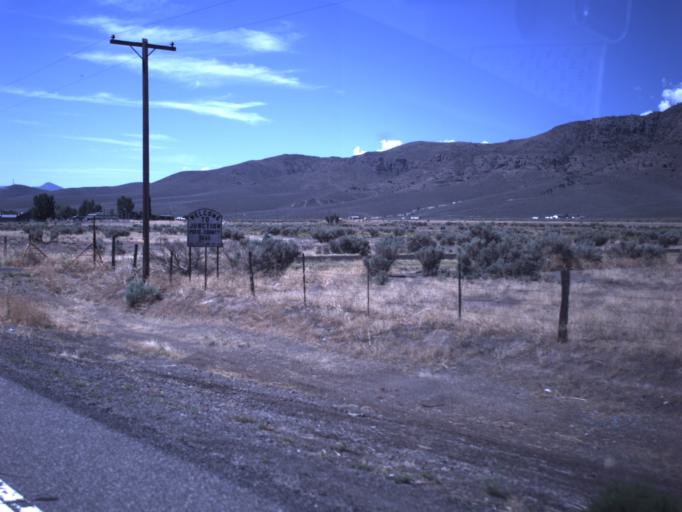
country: US
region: Utah
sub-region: Piute County
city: Junction
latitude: 38.2509
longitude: -112.2203
